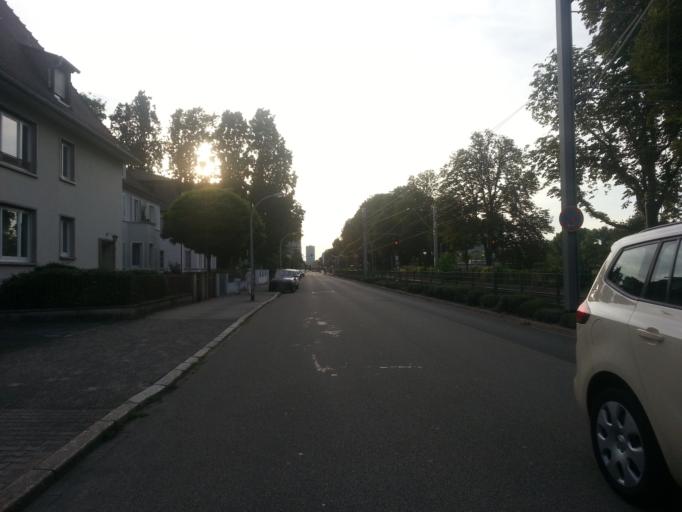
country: DE
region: Baden-Wuerttemberg
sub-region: Karlsruhe Region
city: Mannheim
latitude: 49.4885
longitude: 8.4874
